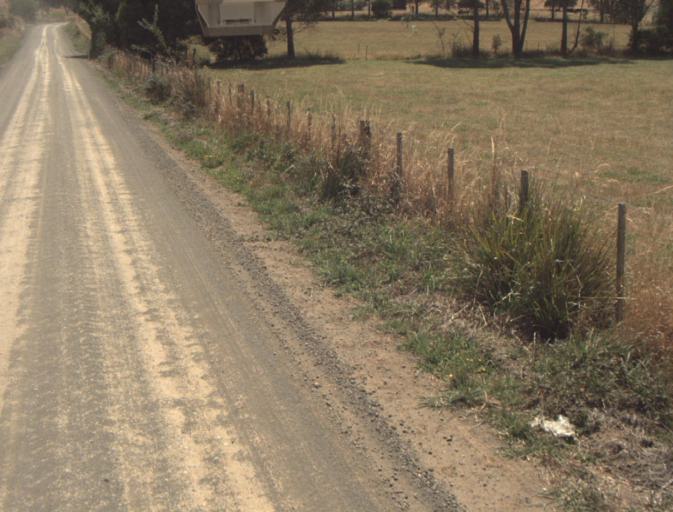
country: AU
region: Tasmania
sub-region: Launceston
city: Mayfield
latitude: -41.2580
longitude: 147.1336
